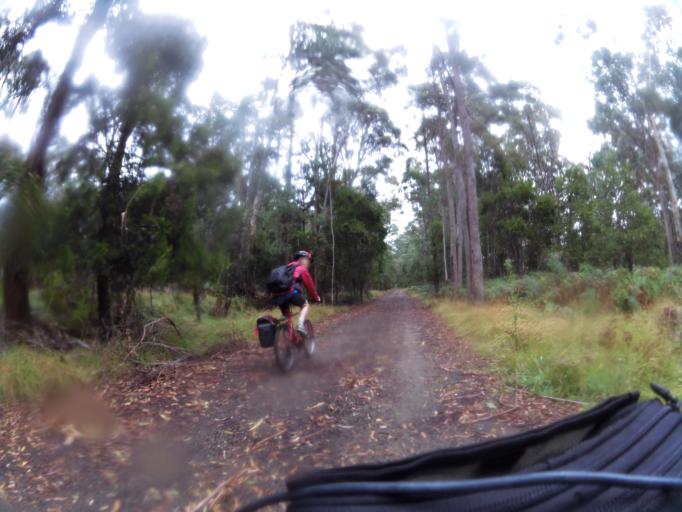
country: AU
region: New South Wales
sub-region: Greater Hume Shire
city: Holbrook
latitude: -36.1916
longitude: 147.5406
